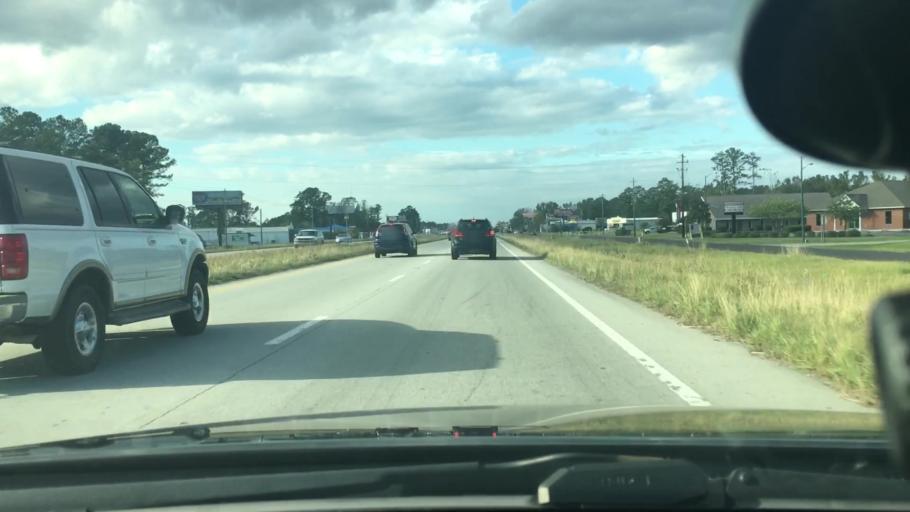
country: US
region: North Carolina
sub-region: Craven County
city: James City
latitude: 35.0610
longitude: -77.0202
